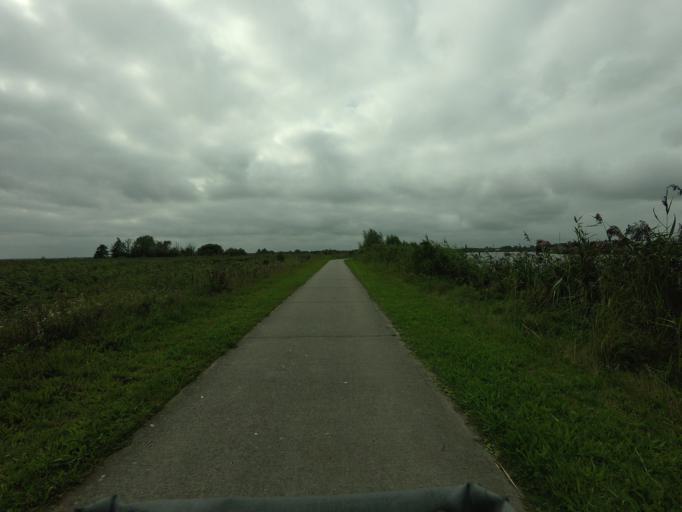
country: NL
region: Overijssel
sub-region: Gemeente Steenwijkerland
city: Giethoorn
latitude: 52.7127
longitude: 6.0685
